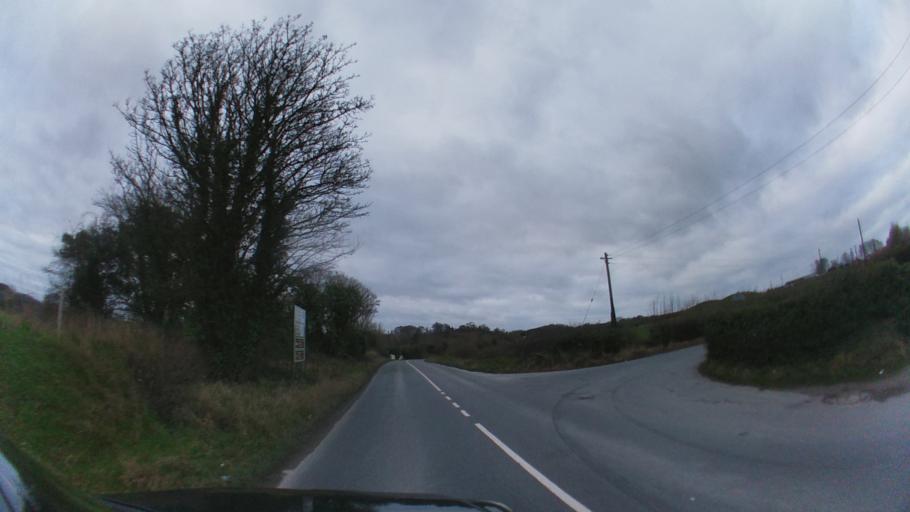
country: IE
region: Leinster
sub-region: Lu
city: Tullyallen
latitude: 53.6978
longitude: -6.3962
